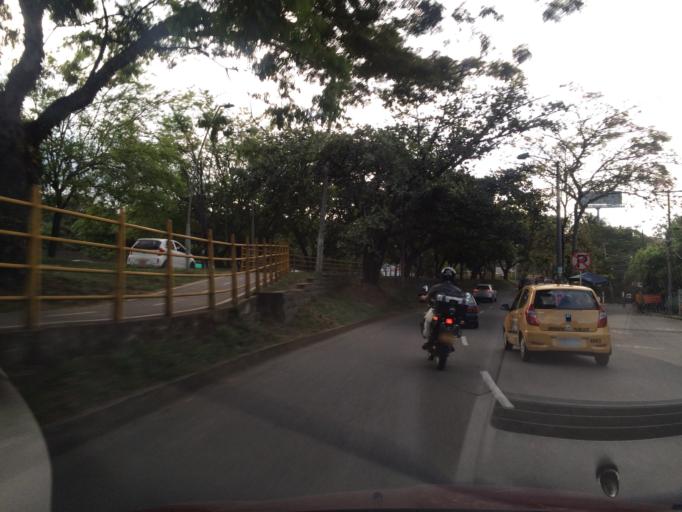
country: CO
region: Valle del Cauca
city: Cali
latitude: 3.3742
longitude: -76.5418
